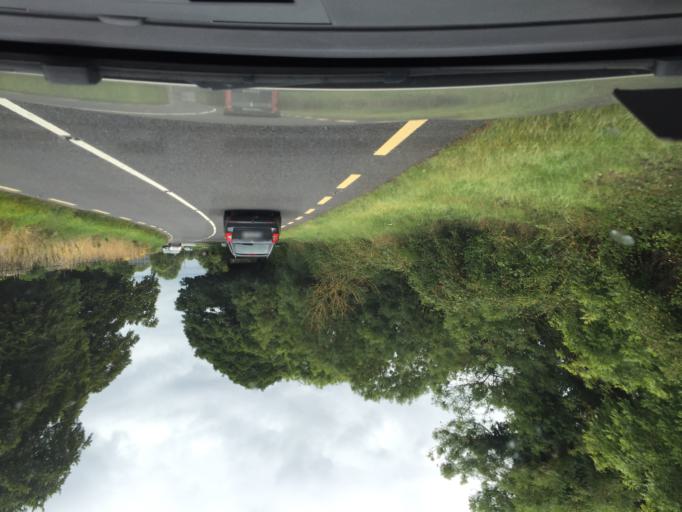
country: IE
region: Leinster
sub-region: Kildare
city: Maynooth
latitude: 53.3803
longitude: -6.5693
